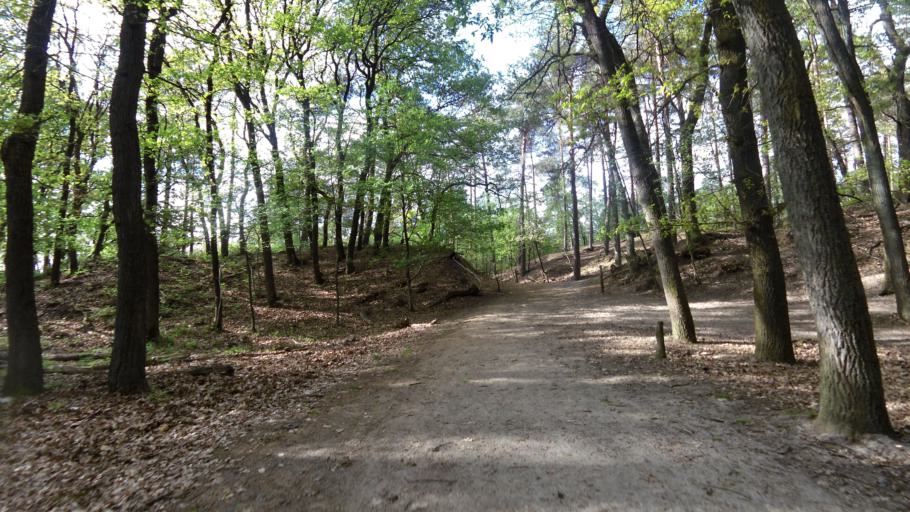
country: NL
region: Gelderland
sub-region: Gemeente Apeldoorn
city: Loenen
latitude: 52.0986
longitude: 5.9858
